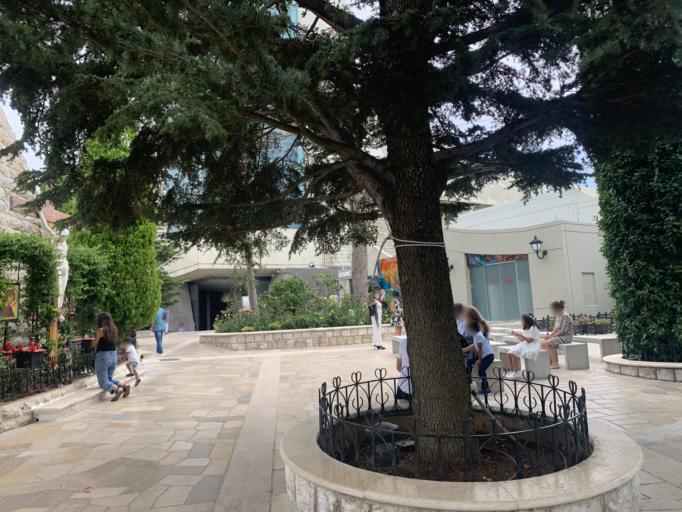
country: LB
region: Mont-Liban
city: Djounie
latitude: 33.9815
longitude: 35.6515
